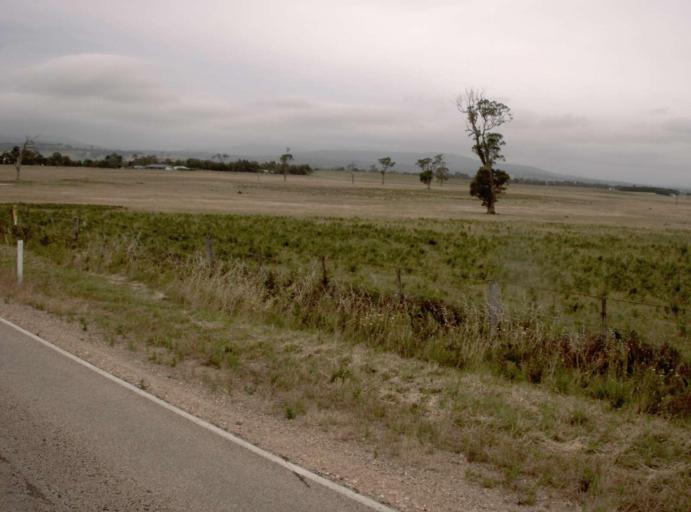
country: AU
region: Victoria
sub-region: East Gippsland
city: Bairnsdale
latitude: -37.8099
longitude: 147.4377
